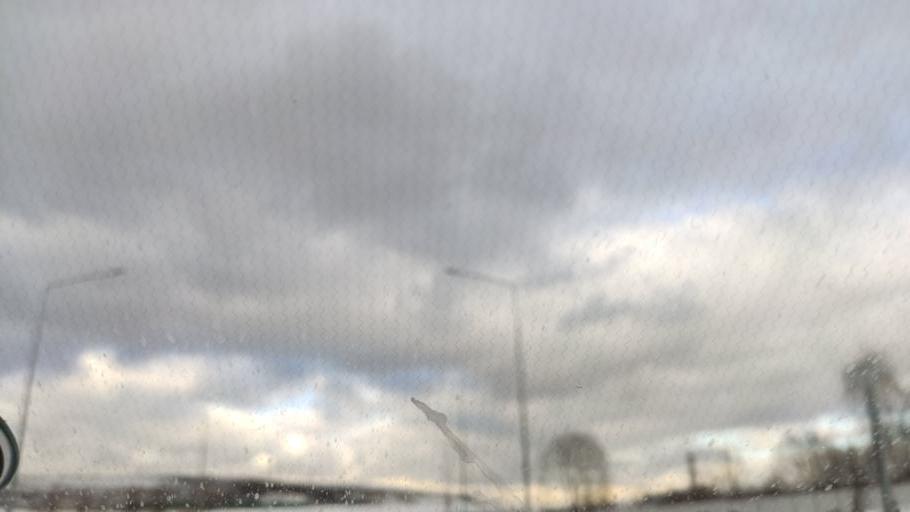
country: RU
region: Moskovskaya
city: Mosrentgen
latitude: 55.6042
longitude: 37.4204
